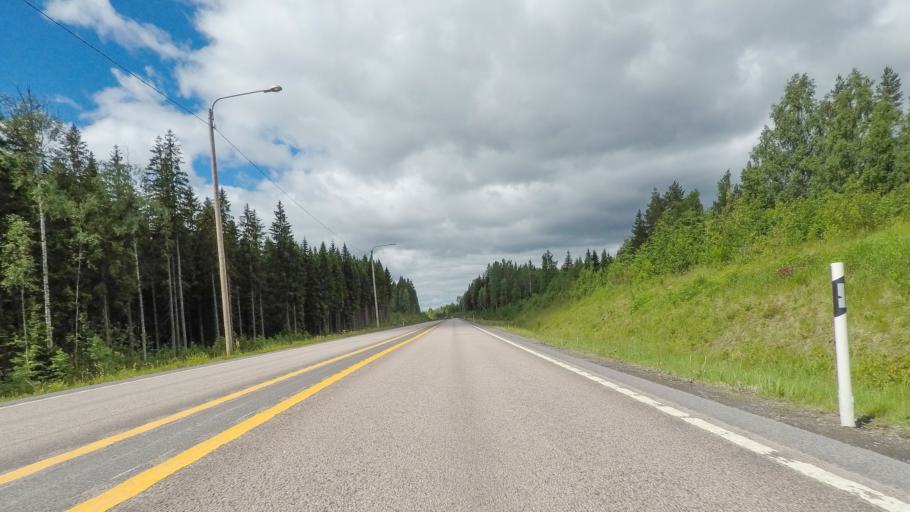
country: FI
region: Paijanne Tavastia
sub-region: Lahti
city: Hartola
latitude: 61.4304
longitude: 26.0092
